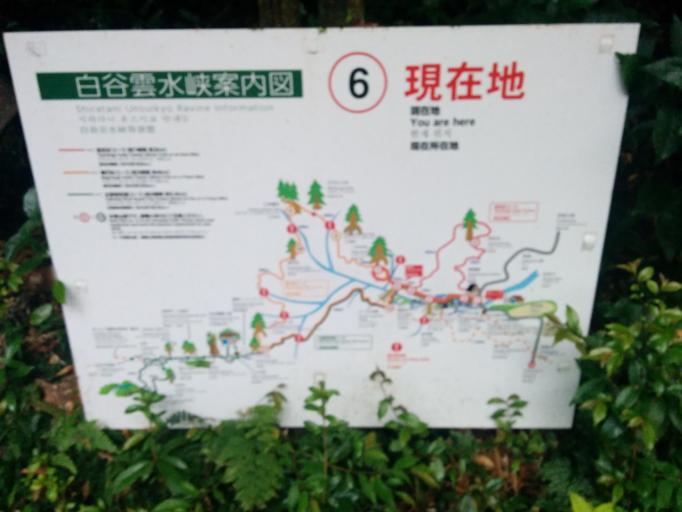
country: JP
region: Kagoshima
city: Nishinoomote
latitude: 30.3774
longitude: 130.5722
